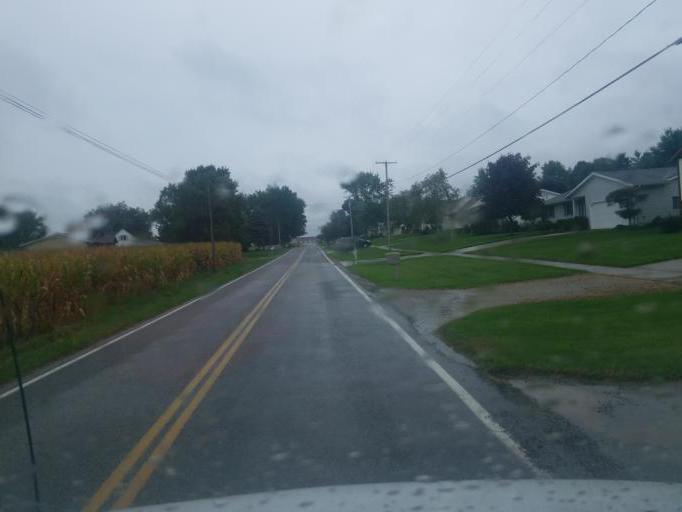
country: US
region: Ohio
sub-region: Wayne County
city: Rittman
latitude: 40.9806
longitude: -81.7999
